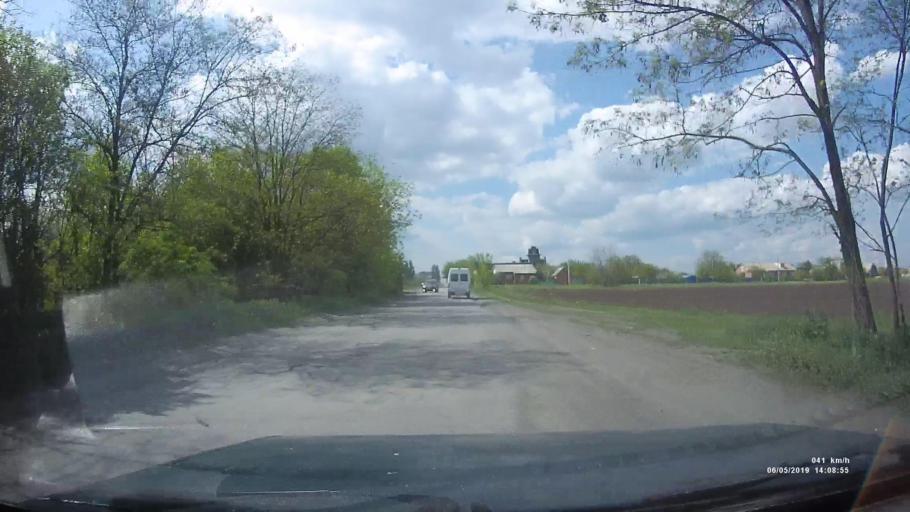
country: RU
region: Rostov
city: Shakhty
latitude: 47.6849
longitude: 40.2943
